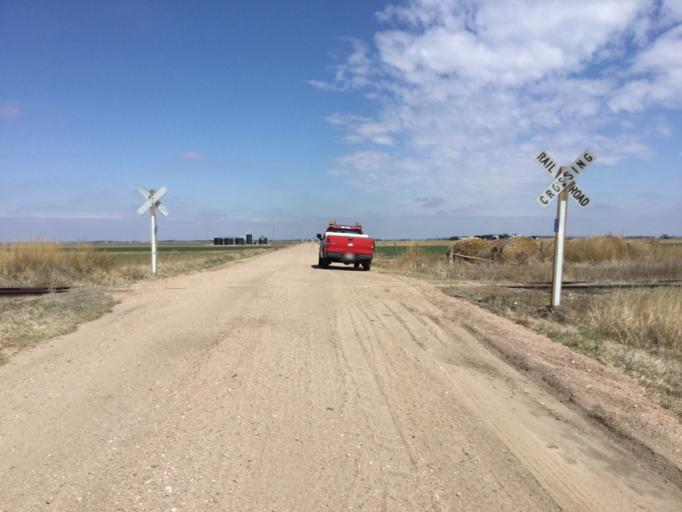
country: US
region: Kansas
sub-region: Barton County
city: Ellinwood
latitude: 38.3519
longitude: -98.5170
